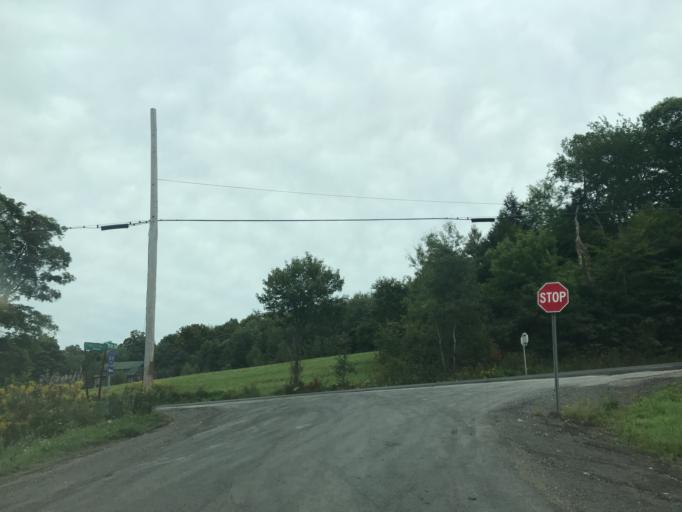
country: US
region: New York
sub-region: Delaware County
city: Stamford
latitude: 42.5314
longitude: -74.6207
